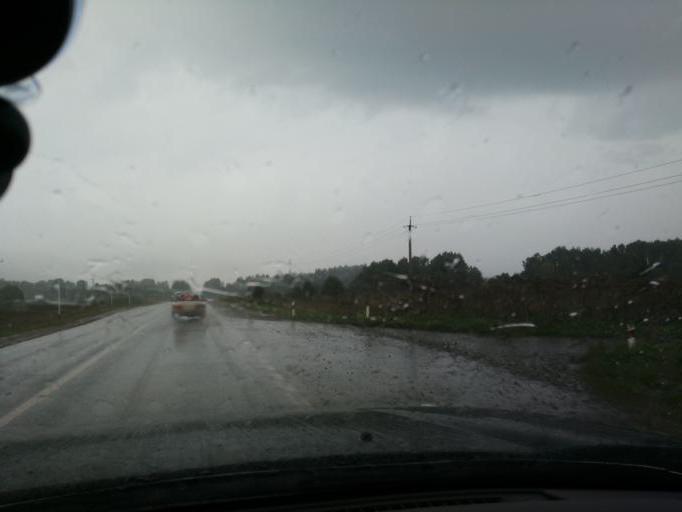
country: RU
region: Perm
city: Osa
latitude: 57.1544
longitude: 55.5297
